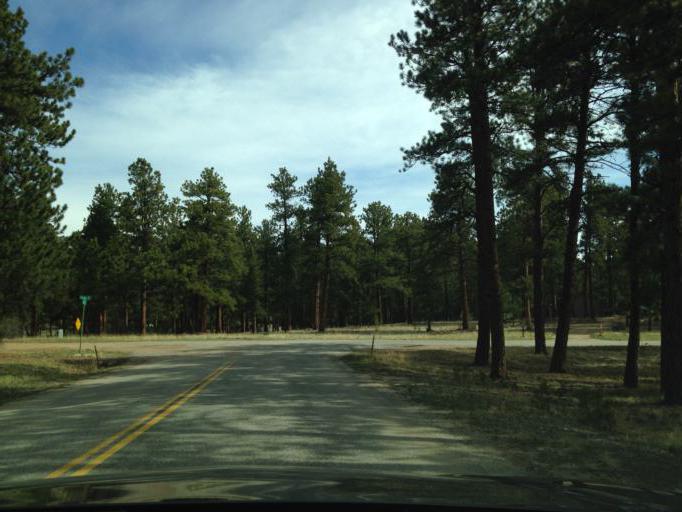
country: US
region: Colorado
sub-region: Jefferson County
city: Evergreen
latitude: 39.4368
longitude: -105.4216
